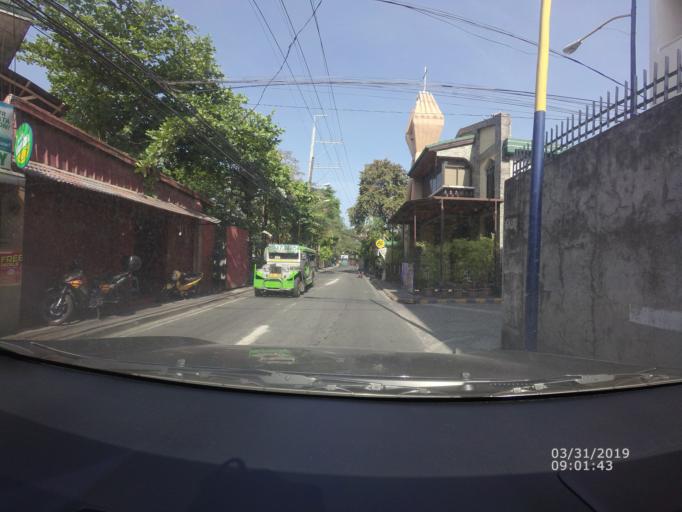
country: PH
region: Metro Manila
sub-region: Mandaluyong
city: Mandaluyong City
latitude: 14.5766
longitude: 121.0239
